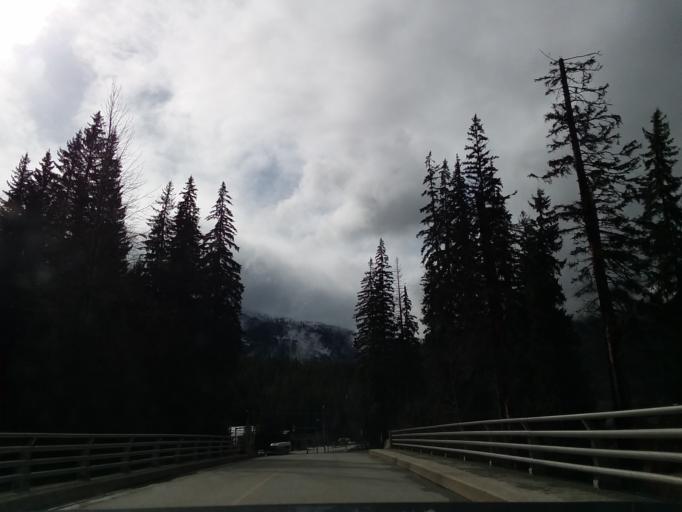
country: CA
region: British Columbia
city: Whistler
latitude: 50.1321
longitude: -122.9515
